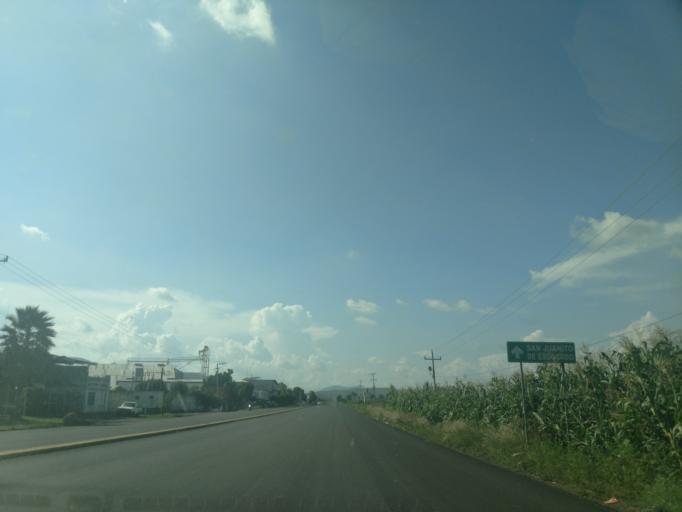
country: MX
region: Jalisco
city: Ahualulco de Mercado
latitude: 20.7083
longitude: -103.9726
